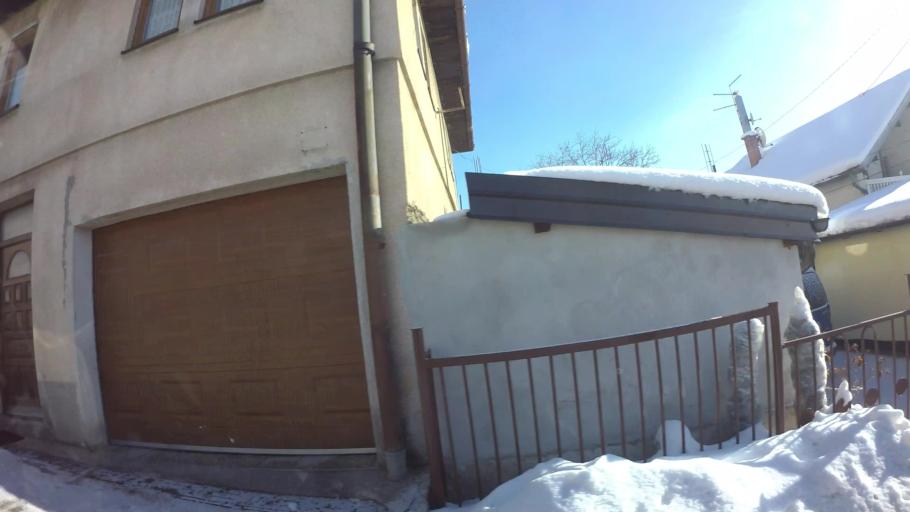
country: BA
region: Federation of Bosnia and Herzegovina
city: Kobilja Glava
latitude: 43.8707
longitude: 18.4280
